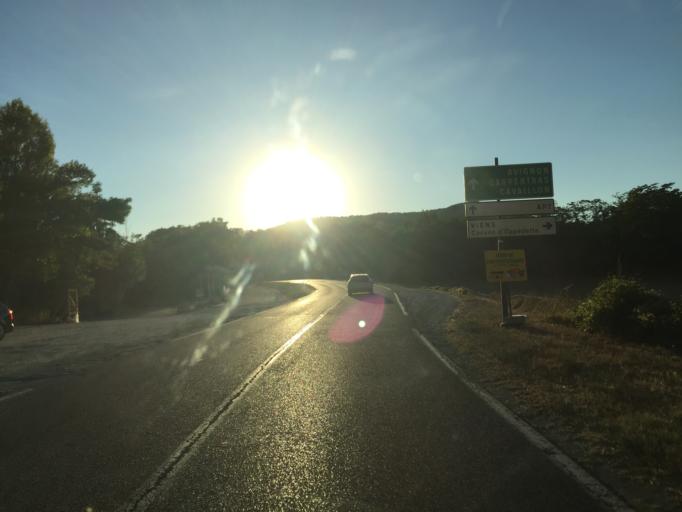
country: FR
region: Provence-Alpes-Cote d'Azur
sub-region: Departement des Alpes-de-Haute-Provence
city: Cereste
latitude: 43.8580
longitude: 5.5593
